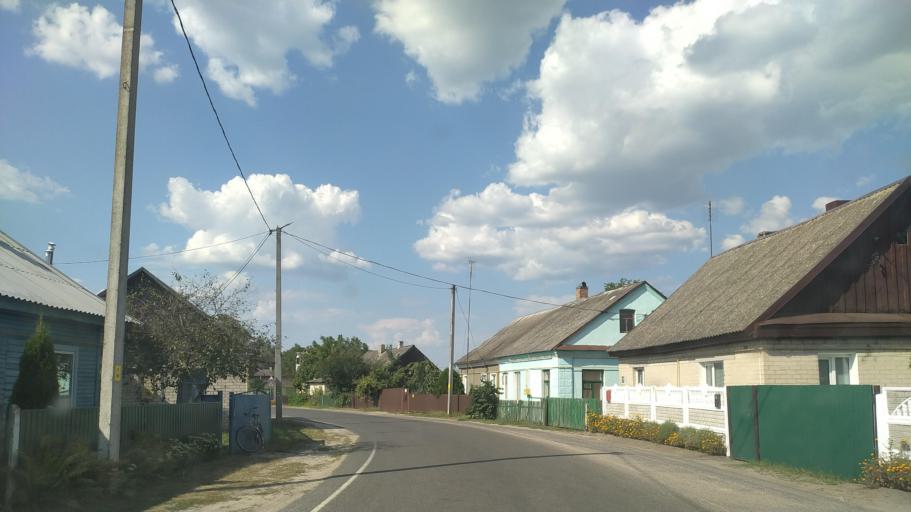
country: BY
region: Brest
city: Drahichyn
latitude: 52.1886
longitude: 25.1478
